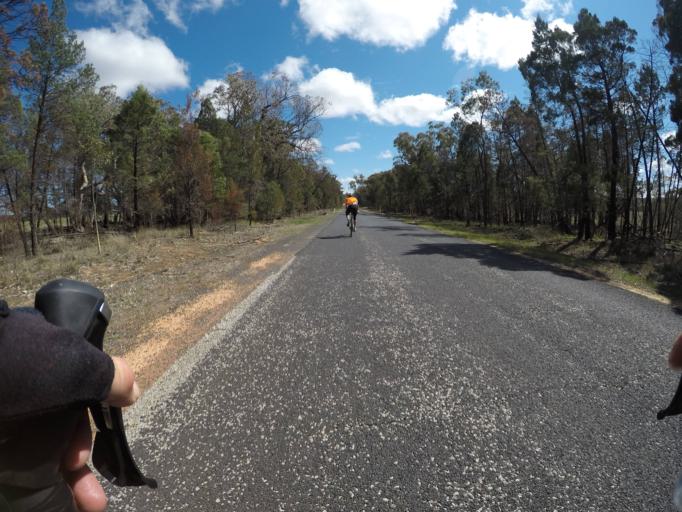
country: AU
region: New South Wales
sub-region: Parkes
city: Peak Hill
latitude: -32.6391
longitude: 148.5497
